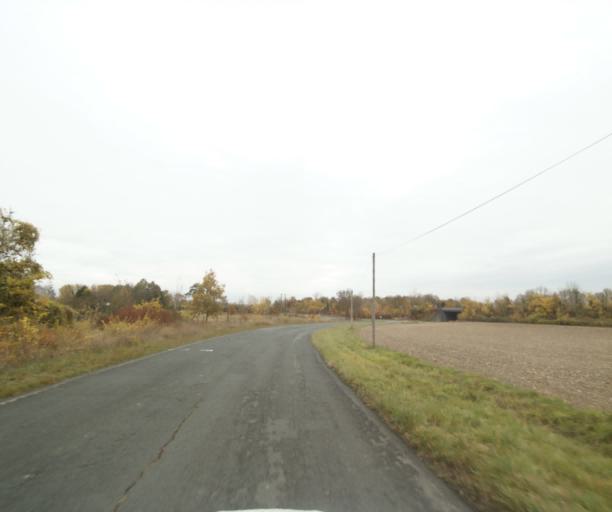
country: FR
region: Poitou-Charentes
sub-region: Departement de la Charente-Maritime
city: Chermignac
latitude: 45.7187
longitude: -0.6613
